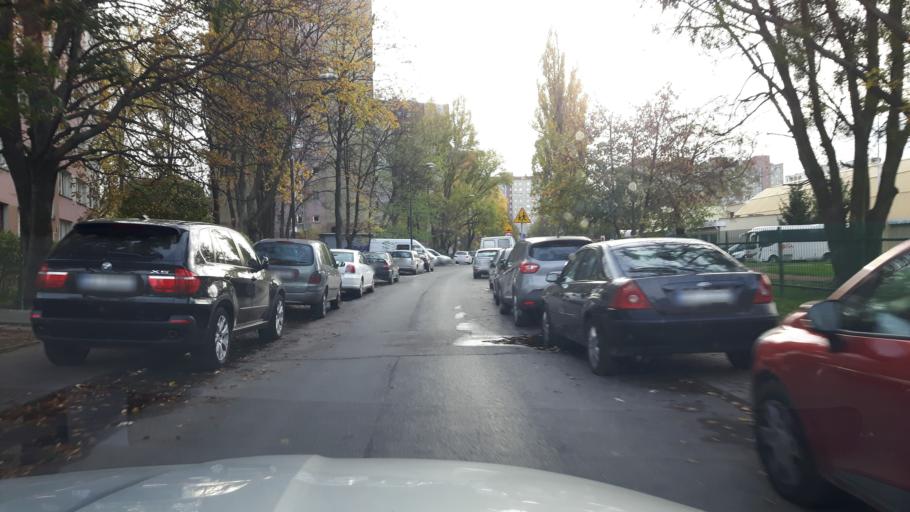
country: PL
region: Masovian Voivodeship
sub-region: Warszawa
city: Ochota
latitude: 52.2053
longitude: 20.9697
